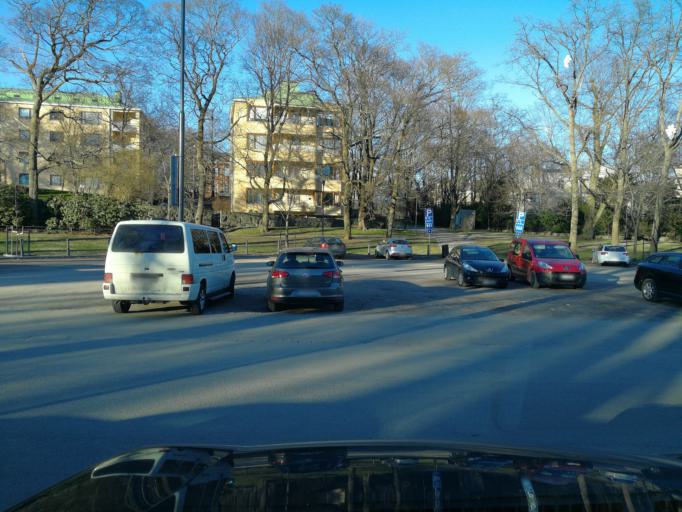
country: FI
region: Uusimaa
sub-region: Helsinki
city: Helsinki
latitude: 60.1578
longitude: 24.9562
